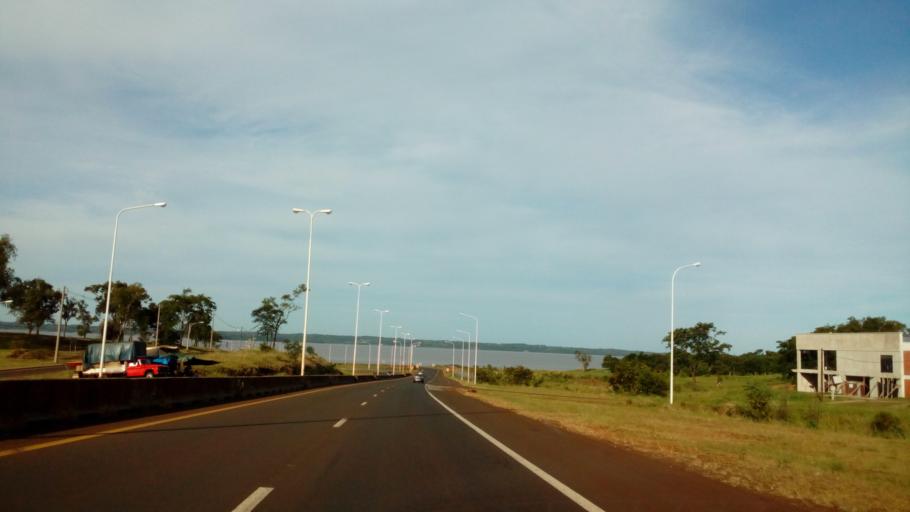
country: AR
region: Misiones
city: Garupa
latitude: -27.4467
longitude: -55.8507
